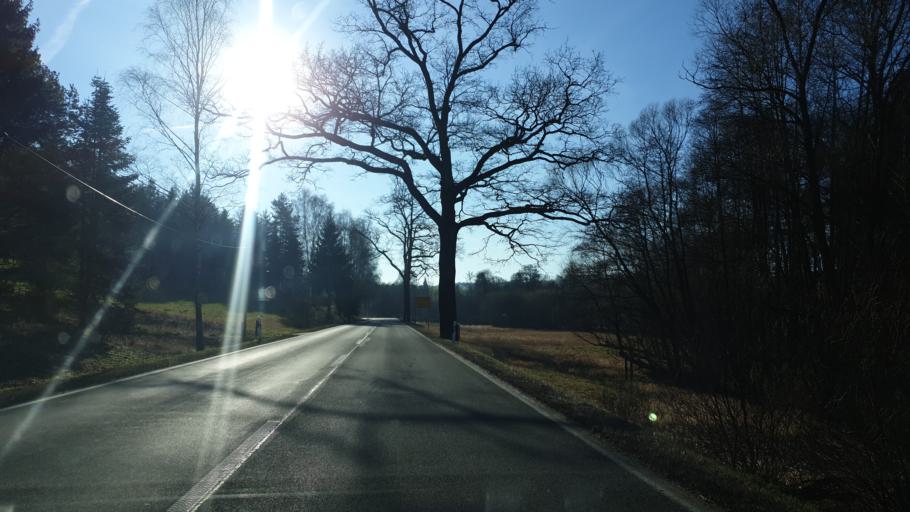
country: DE
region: Saxony
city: Bad Brambach
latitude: 50.2621
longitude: 12.3007
